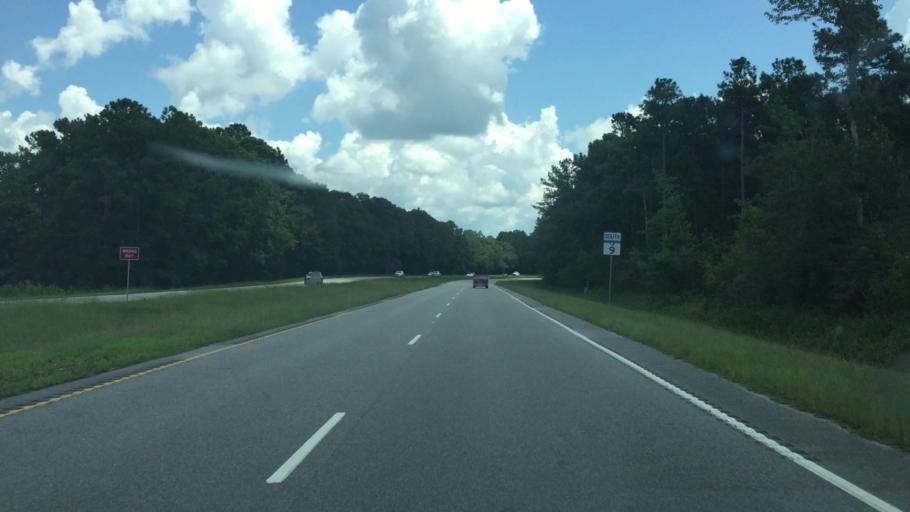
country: US
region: South Carolina
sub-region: Horry County
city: Loris
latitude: 34.0333
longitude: -78.8072
